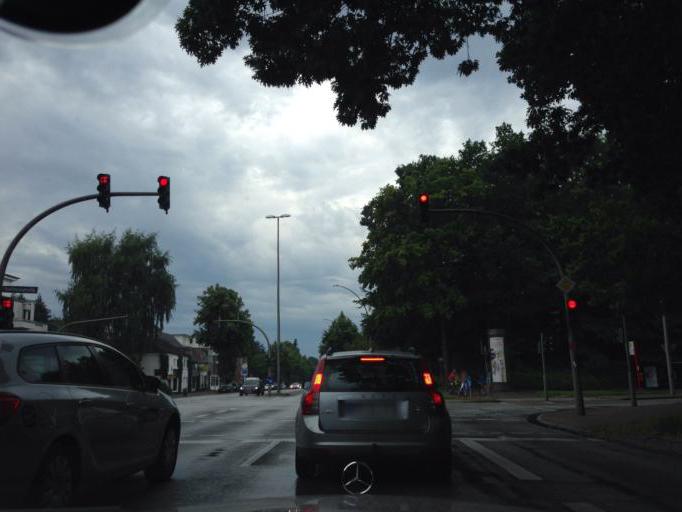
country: DE
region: Hamburg
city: Wellingsbuettel
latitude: 53.6395
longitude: 10.0951
